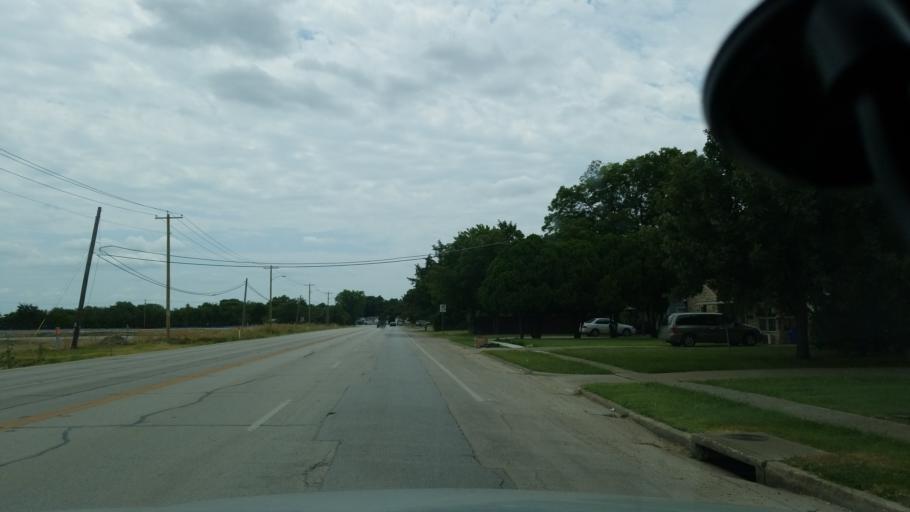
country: US
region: Texas
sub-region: Dallas County
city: Grand Prairie
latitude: 32.7408
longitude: -96.9878
